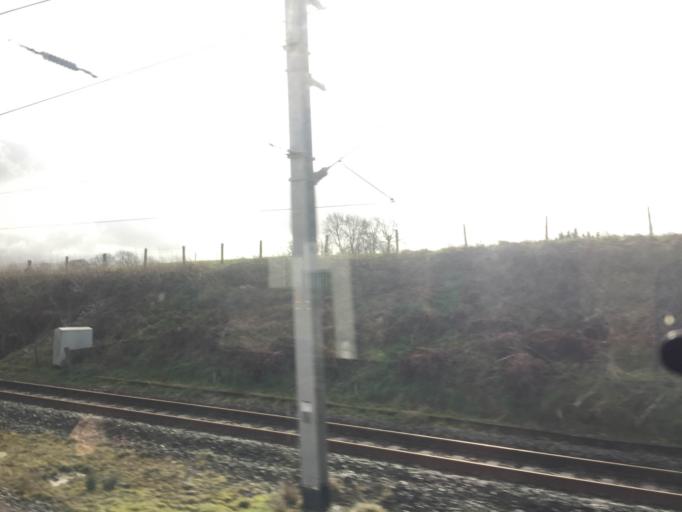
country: GB
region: England
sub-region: Cumbria
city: Sedbergh
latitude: 54.3583
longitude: -2.6191
